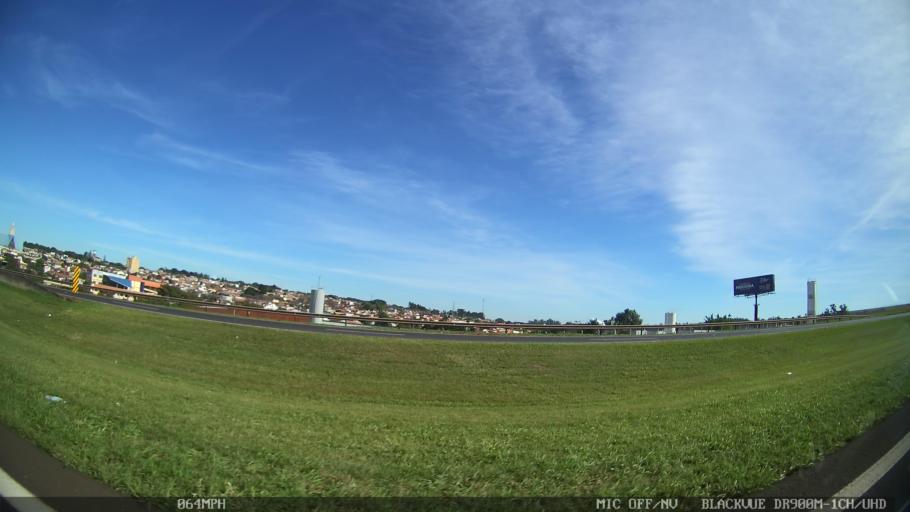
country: BR
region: Sao Paulo
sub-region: Araras
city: Araras
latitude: -22.3474
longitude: -47.3940
